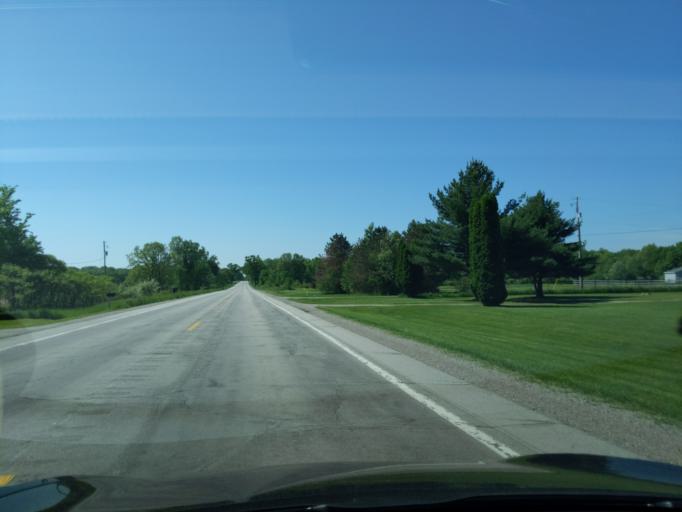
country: US
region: Michigan
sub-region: Ingham County
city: Stockbridge
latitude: 42.4956
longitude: -84.1902
